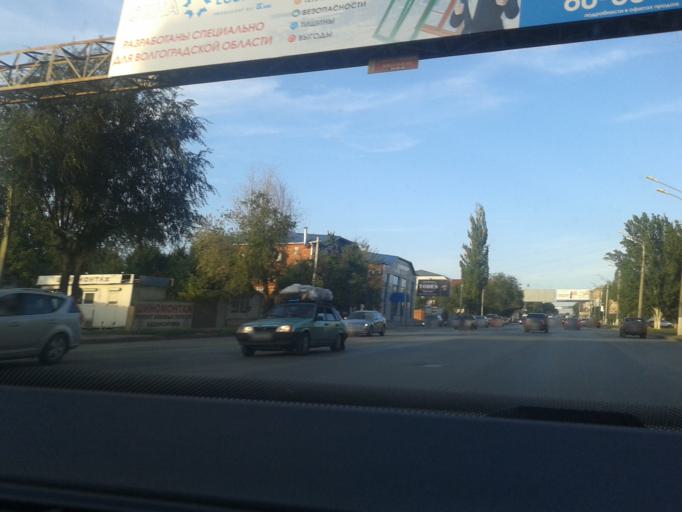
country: RU
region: Volgograd
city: Volgograd
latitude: 48.7149
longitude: 44.4995
